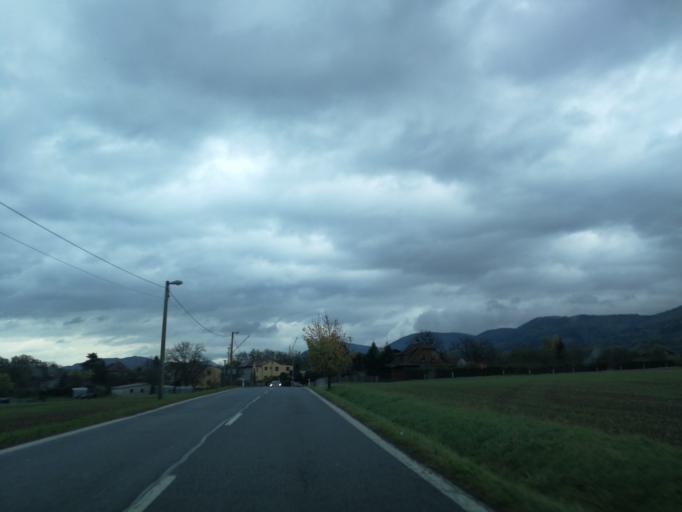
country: CZ
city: Hodslavice
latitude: 49.5362
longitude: 18.0383
